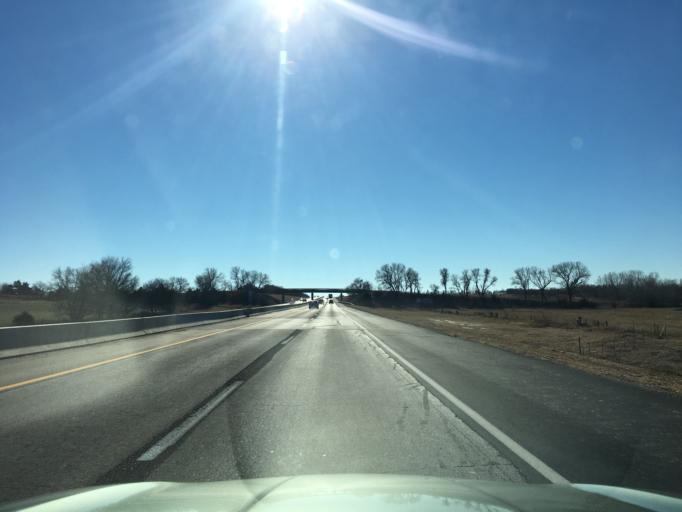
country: US
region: Kansas
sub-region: Sumner County
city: Wellington
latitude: 37.0892
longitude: -97.3387
